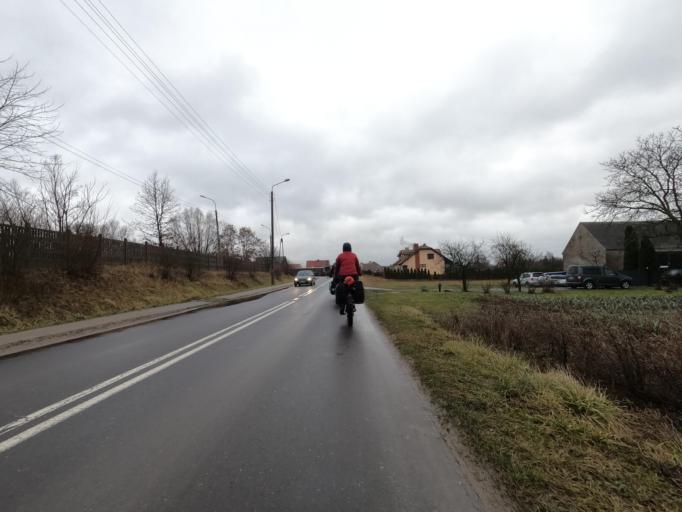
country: PL
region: Greater Poland Voivodeship
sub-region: Powiat pilski
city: Osiek nad Notecia
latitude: 53.1193
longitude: 17.2838
